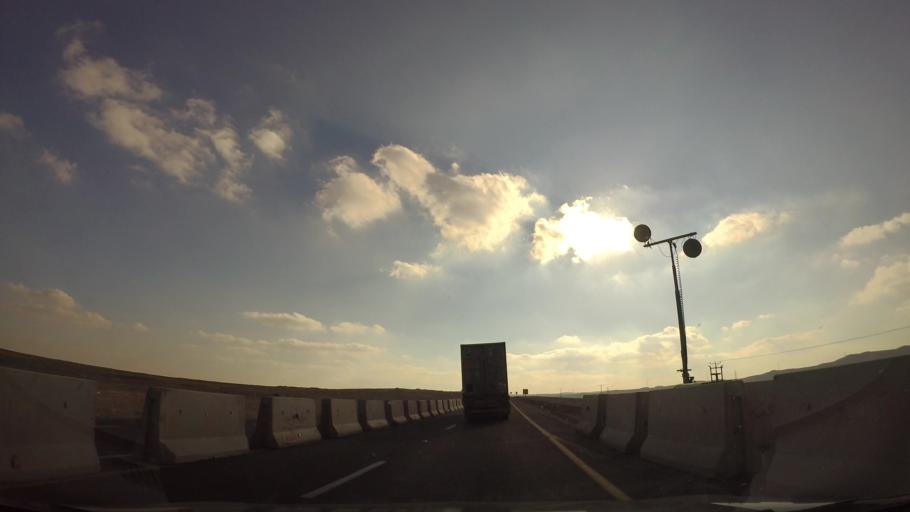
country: JO
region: Karak
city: Karak City
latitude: 31.1288
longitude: 36.0224
